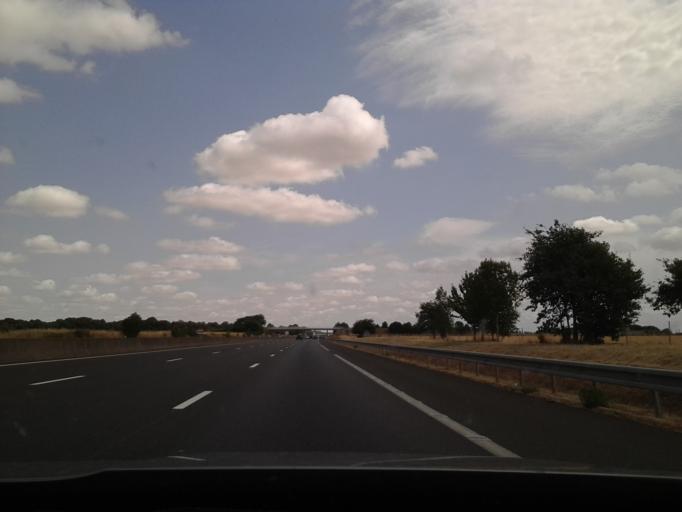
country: FR
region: Centre
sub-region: Departement d'Indre-et-Loire
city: Monnaie
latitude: 47.4847
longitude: 0.7997
